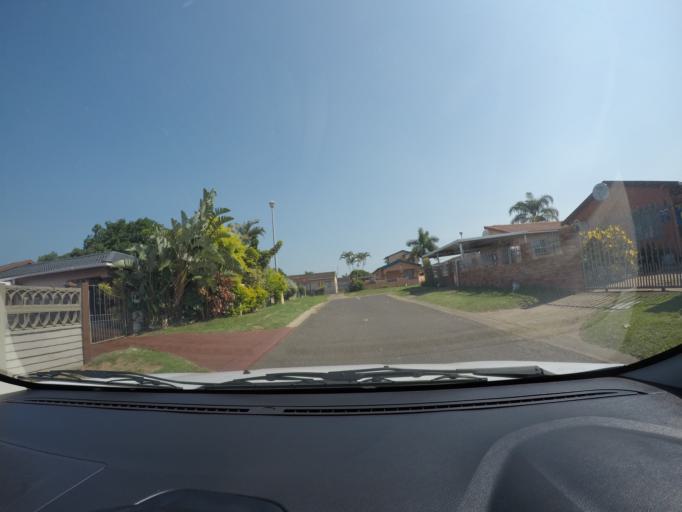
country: ZA
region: KwaZulu-Natal
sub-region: uThungulu District Municipality
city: Richards Bay
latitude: -28.7216
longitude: 32.0439
